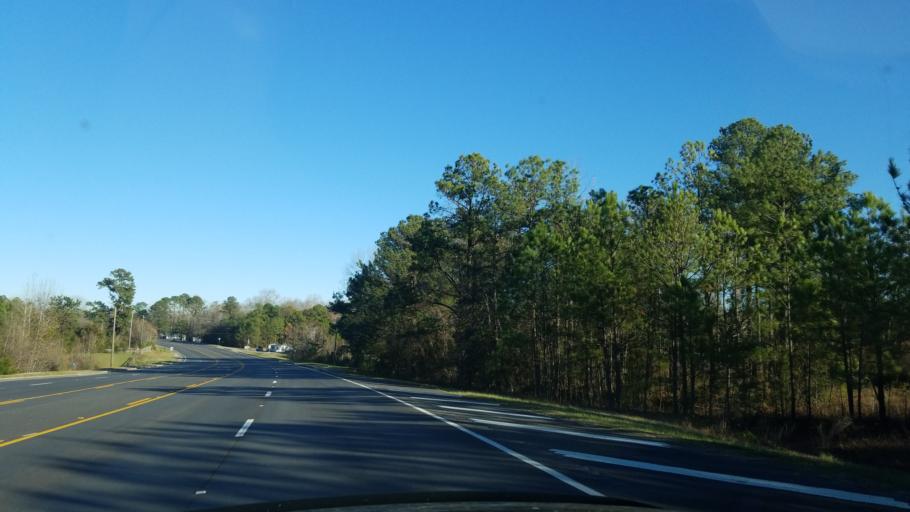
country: US
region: Georgia
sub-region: Talbot County
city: Talbotton
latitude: 32.5749
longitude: -84.5643
